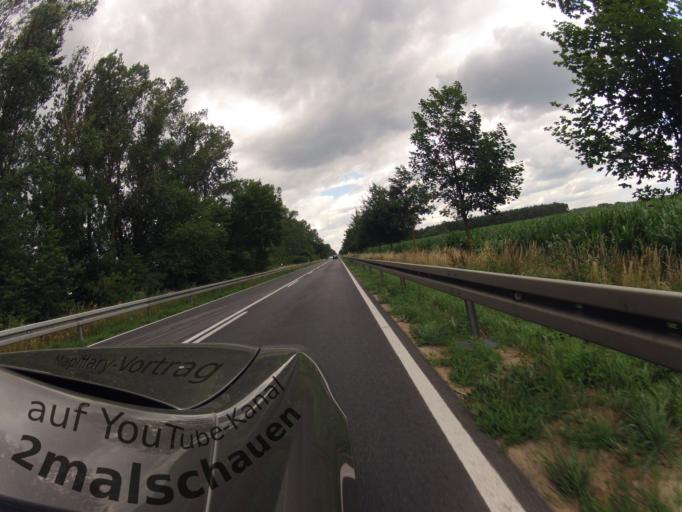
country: DE
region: Mecklenburg-Vorpommern
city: Anklam
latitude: 53.8101
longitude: 13.7331
